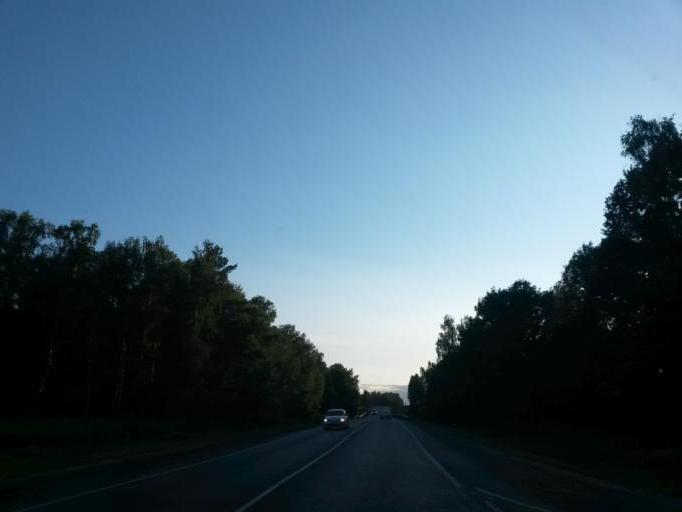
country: RU
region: Moskovskaya
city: Vostryakovo
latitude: 55.3325
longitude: 37.7279
